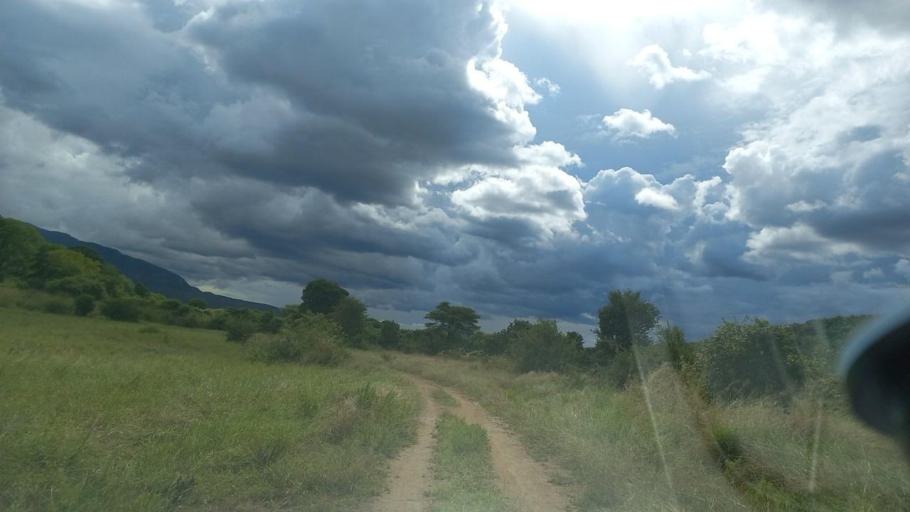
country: ZM
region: Lusaka
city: Luangwa
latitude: -15.6521
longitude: 30.3534
